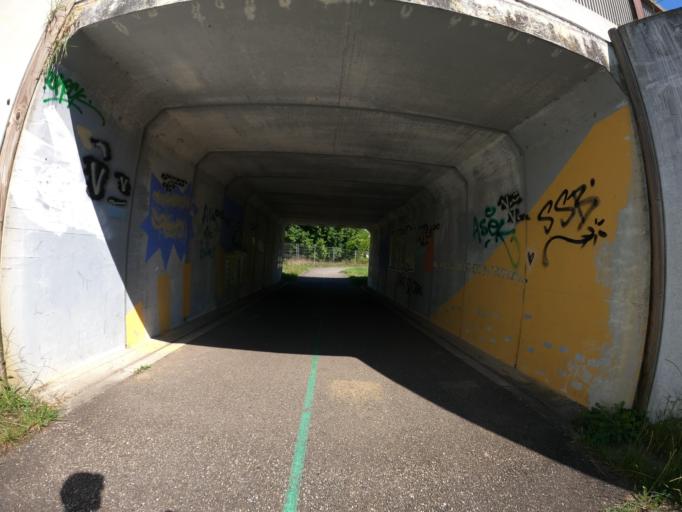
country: FR
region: Aquitaine
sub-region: Departement du Lot-et-Garonne
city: Bias
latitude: 44.4017
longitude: 0.6728
